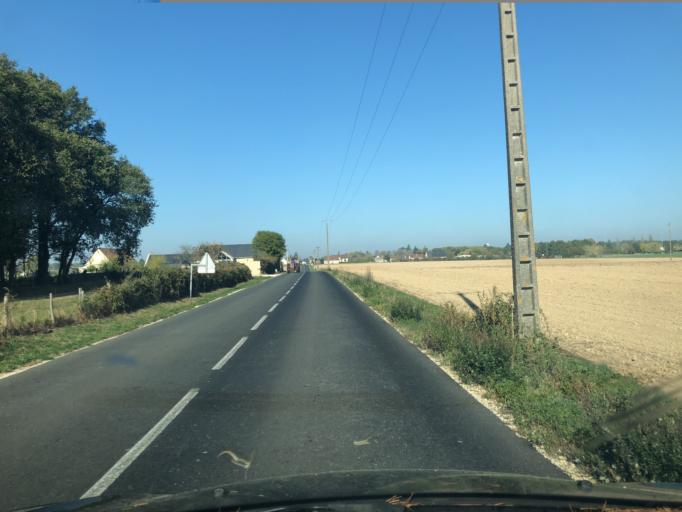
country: FR
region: Centre
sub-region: Departement d'Indre-et-Loire
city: Rouziers-de-Touraine
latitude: 47.5085
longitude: 0.6505
